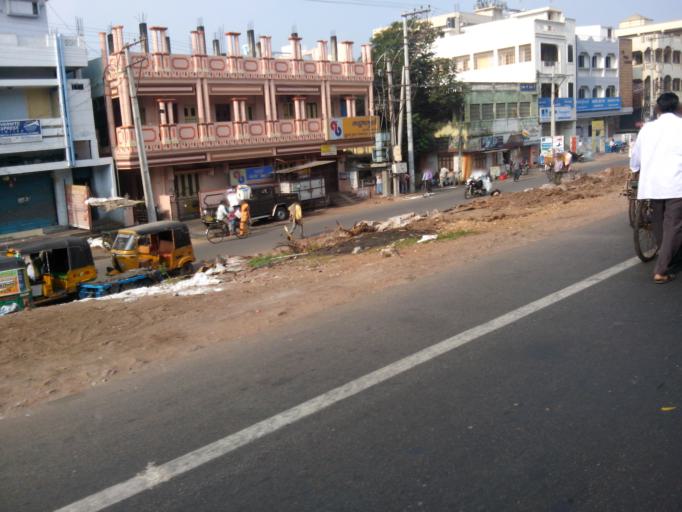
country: IN
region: Andhra Pradesh
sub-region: Krishna
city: Vijayawada
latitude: 16.5077
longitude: 80.6244
